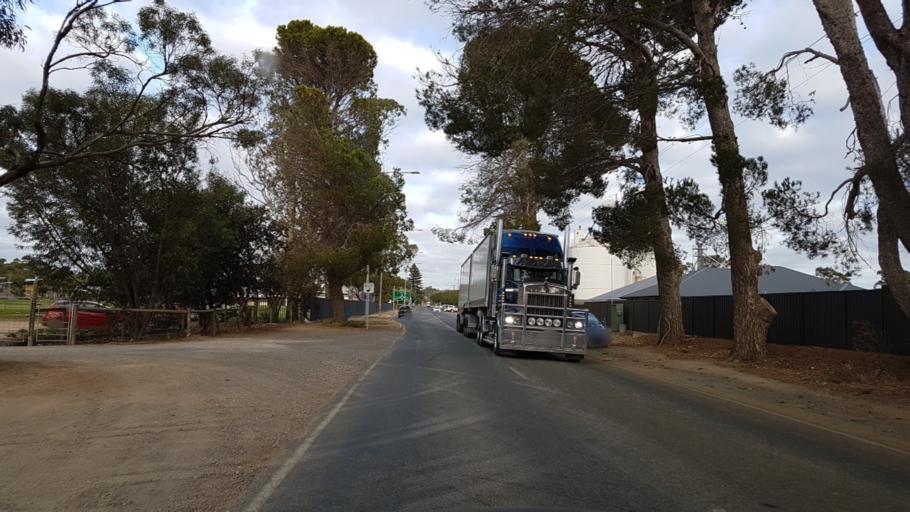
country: AU
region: South Australia
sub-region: Alexandrina
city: Strathalbyn
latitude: -35.2566
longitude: 138.9027
